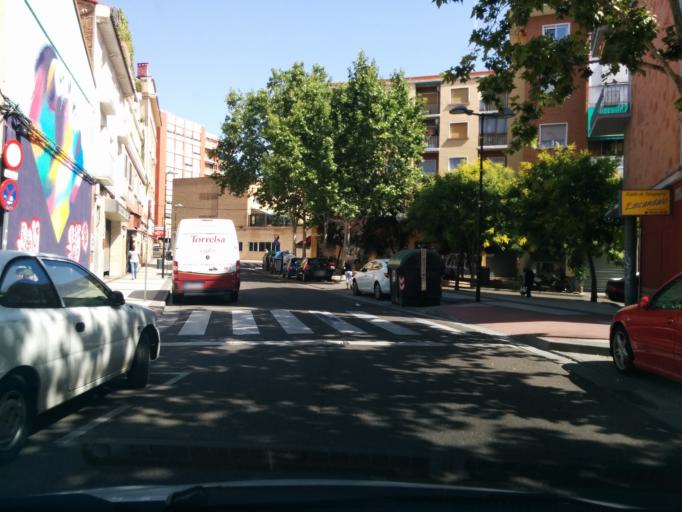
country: ES
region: Aragon
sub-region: Provincia de Zaragoza
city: Zaragoza
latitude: 41.6317
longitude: -0.8844
